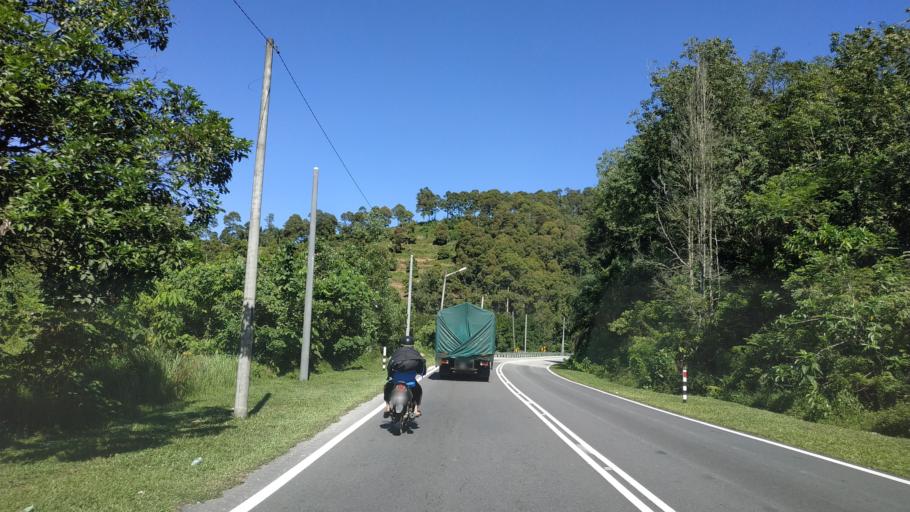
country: MY
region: Kedah
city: Kulim
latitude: 5.3265
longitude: 100.5325
